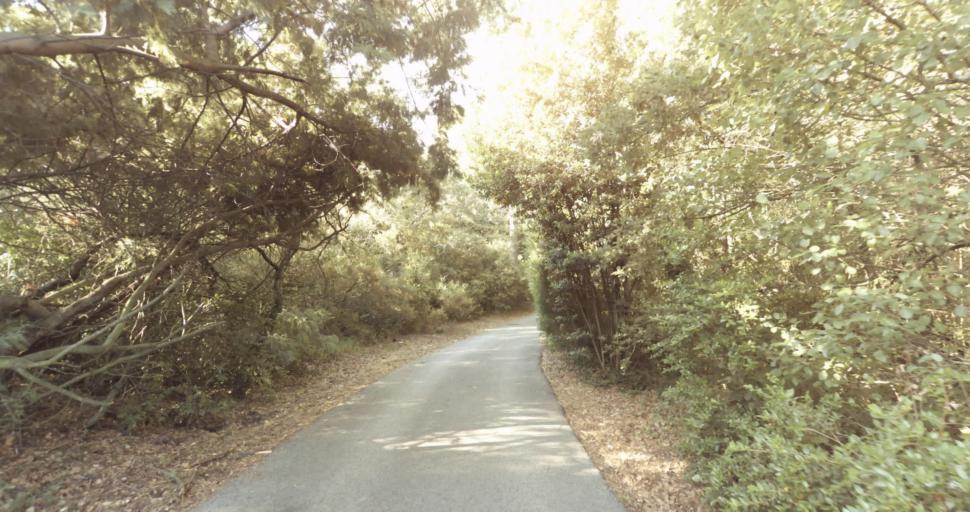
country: FR
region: Provence-Alpes-Cote d'Azur
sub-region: Departement du Var
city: Saint-Tropez
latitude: 43.2562
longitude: 6.6273
